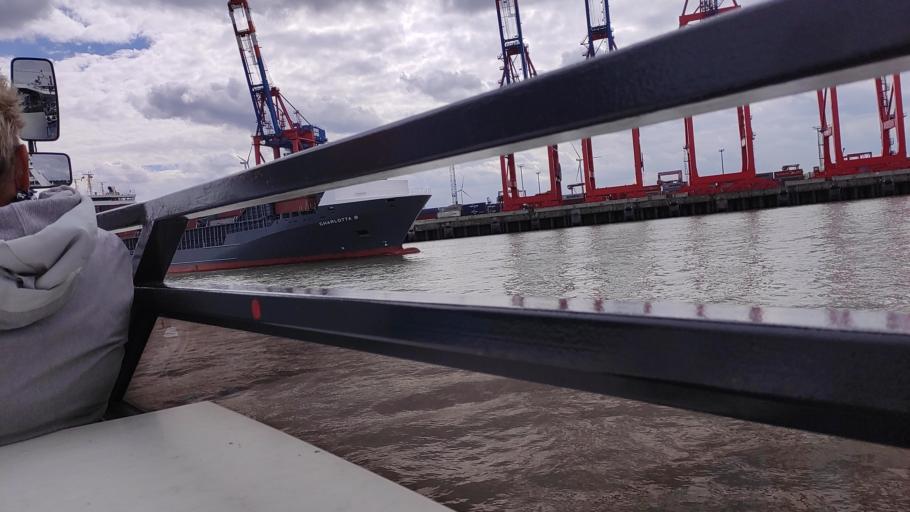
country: DE
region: Hamburg
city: Altona
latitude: 53.5359
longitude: 9.9066
